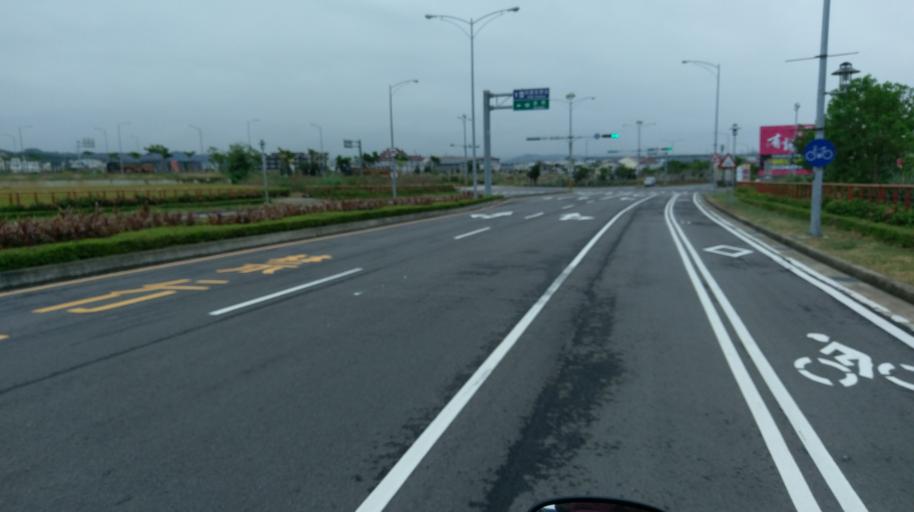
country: TW
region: Taiwan
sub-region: Miaoli
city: Miaoli
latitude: 24.6157
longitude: 120.8250
